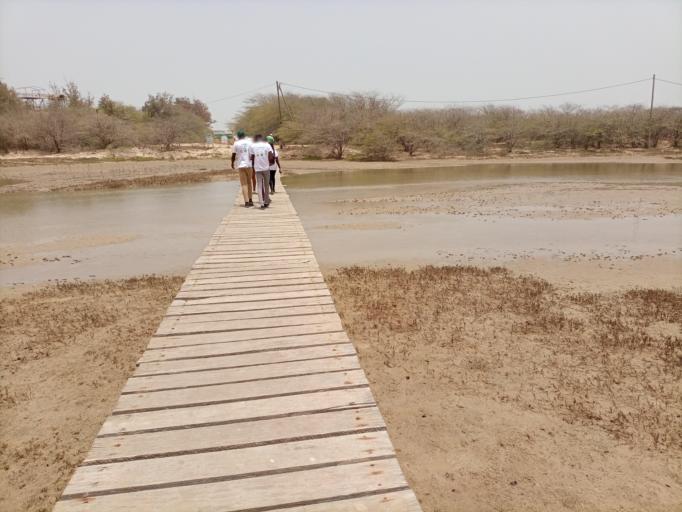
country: SN
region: Saint-Louis
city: Saint-Louis
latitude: 15.8656
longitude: -16.5107
